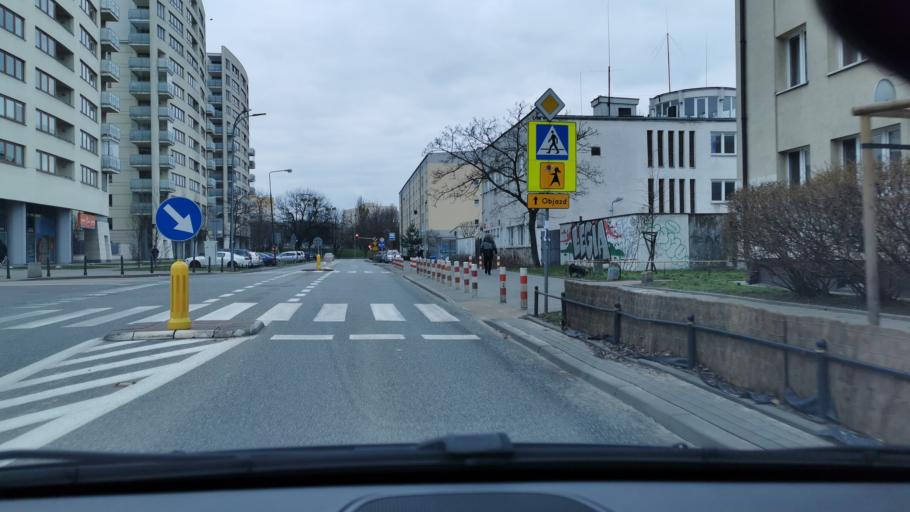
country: PL
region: Masovian Voivodeship
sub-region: Warszawa
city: Ochota
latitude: 52.2028
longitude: 20.9744
